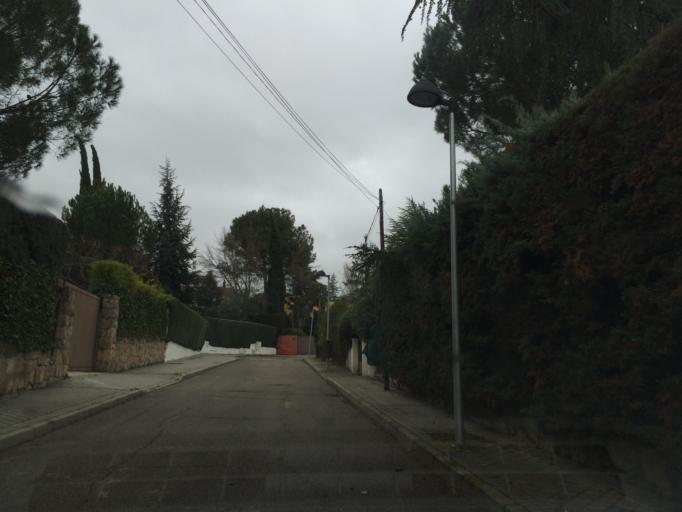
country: ES
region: Madrid
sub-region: Provincia de Madrid
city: Tres Cantos
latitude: 40.6108
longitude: -3.6869
